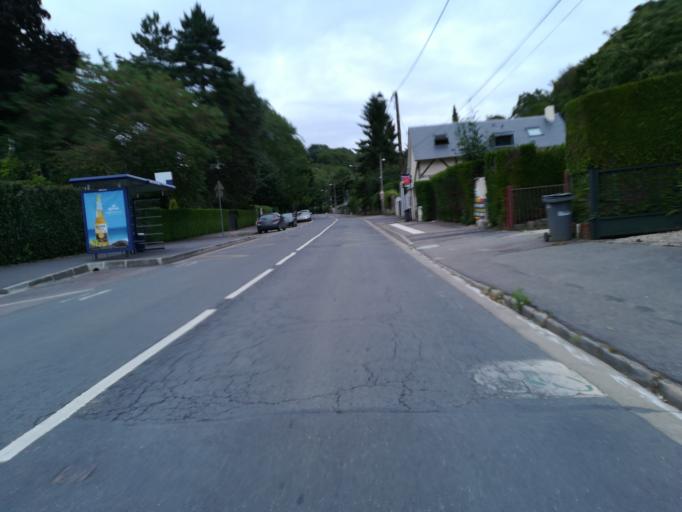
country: FR
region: Haute-Normandie
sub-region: Departement de la Seine-Maritime
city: Mont-Saint-Aignan
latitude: 49.4622
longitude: 1.0890
